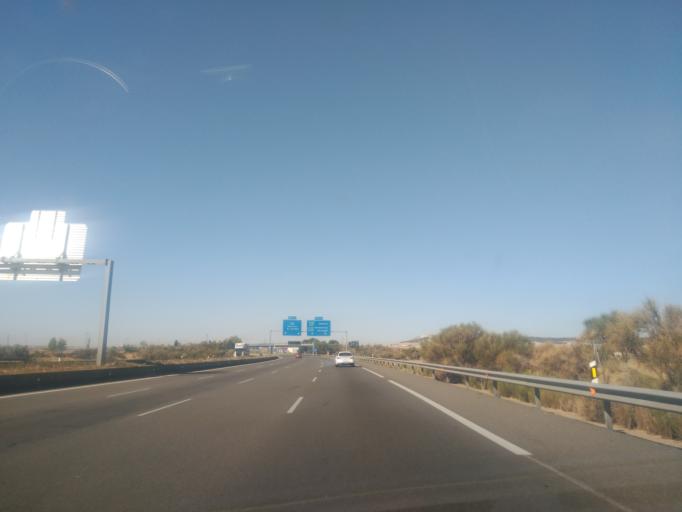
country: ES
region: Castille and Leon
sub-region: Provincia de Valladolid
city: Tordesillas
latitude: 41.5127
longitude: -4.9973
